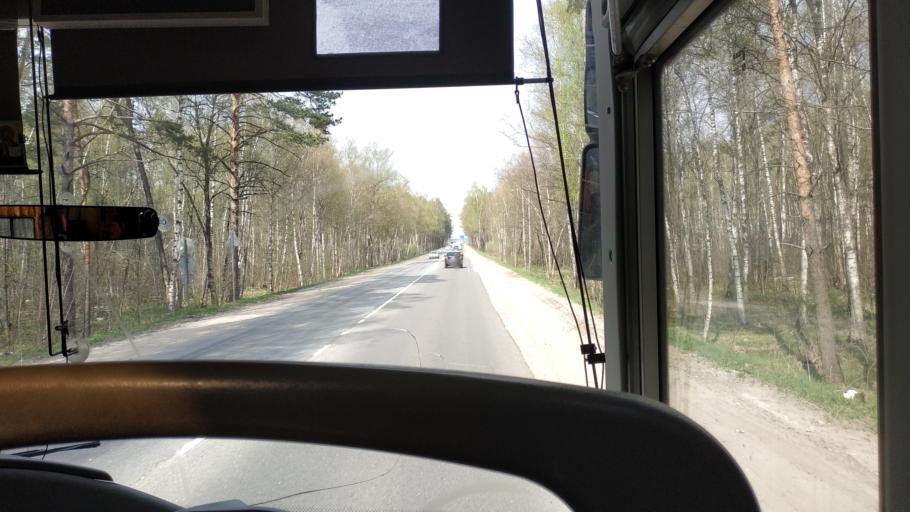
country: RU
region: Moskovskaya
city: Lytkarino
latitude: 55.6057
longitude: 37.9169
